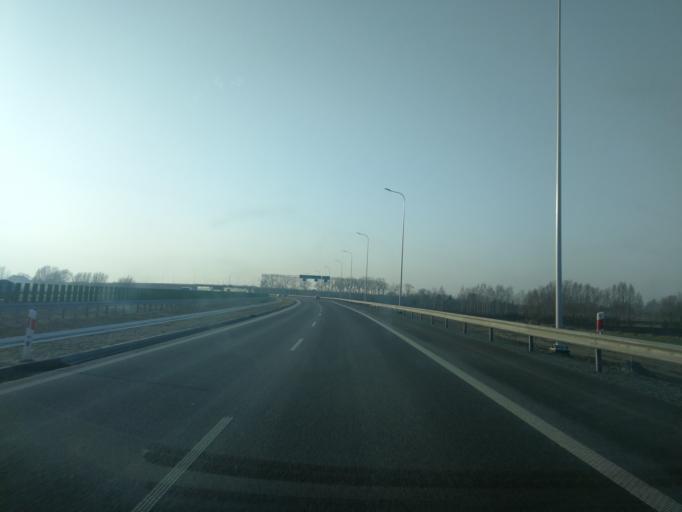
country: PL
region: Warmian-Masurian Voivodeship
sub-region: Powiat elblaski
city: Elblag
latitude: 54.1623
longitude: 19.3536
